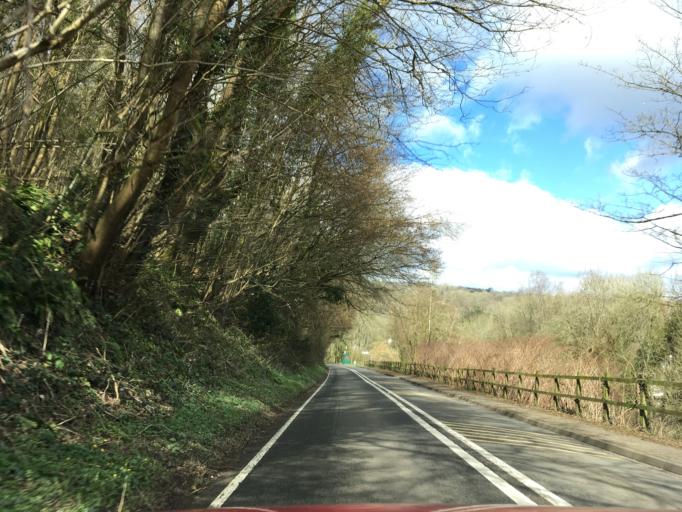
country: GB
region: Wales
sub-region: Monmouthshire
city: Tintern
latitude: 51.7055
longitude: -2.6702
